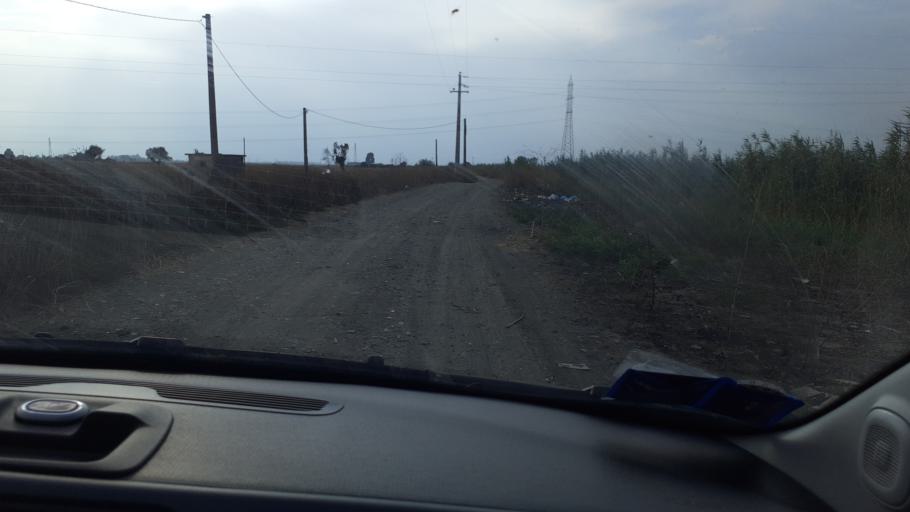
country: IT
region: Sicily
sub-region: Catania
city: Catania
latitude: 37.4323
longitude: 15.0148
